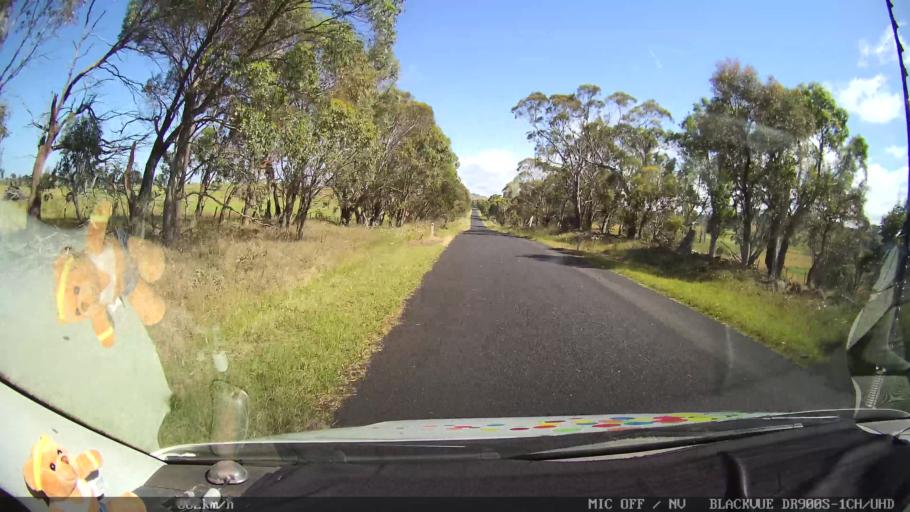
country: AU
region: New South Wales
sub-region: Guyra
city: Guyra
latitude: -30.0869
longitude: 151.6779
